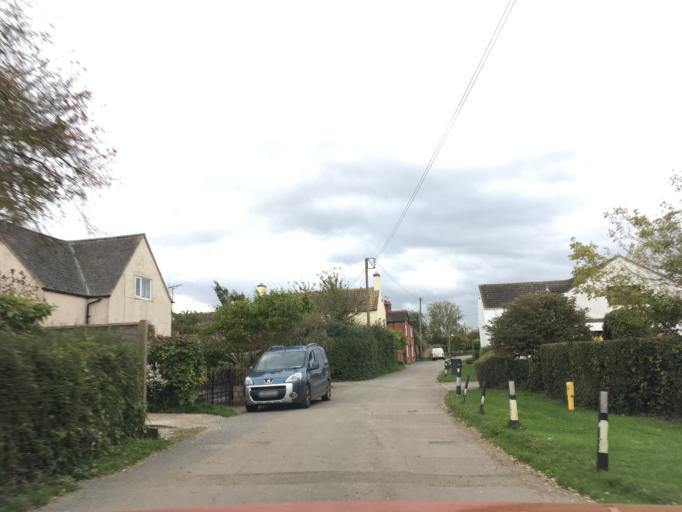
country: GB
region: England
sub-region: Gloucestershire
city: Stonehouse
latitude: 51.7610
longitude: -2.3069
